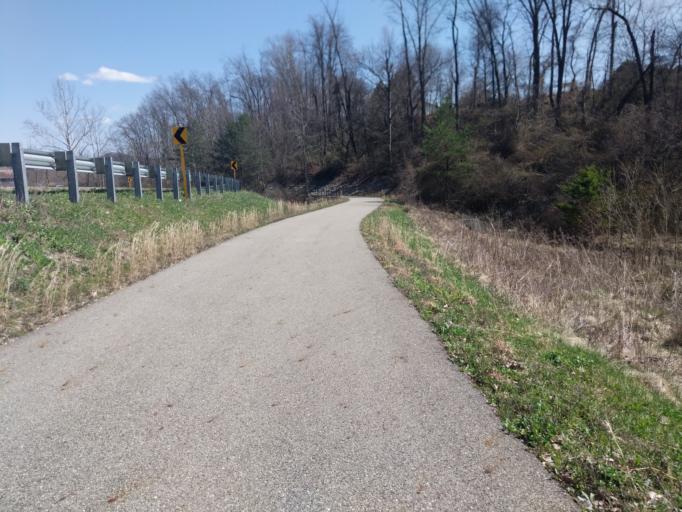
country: US
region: Ohio
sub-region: Athens County
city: The Plains
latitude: 39.3650
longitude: -82.1210
